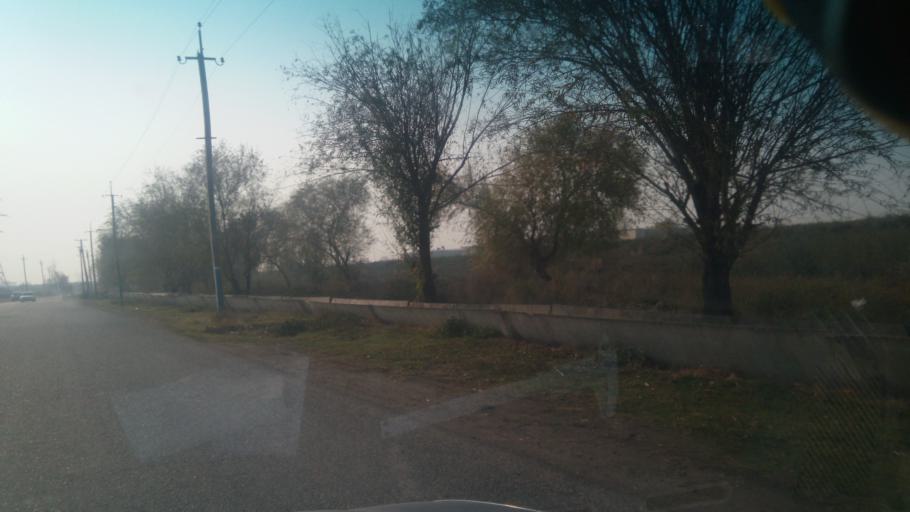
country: UZ
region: Sirdaryo
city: Guliston
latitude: 40.5153
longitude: 68.7754
